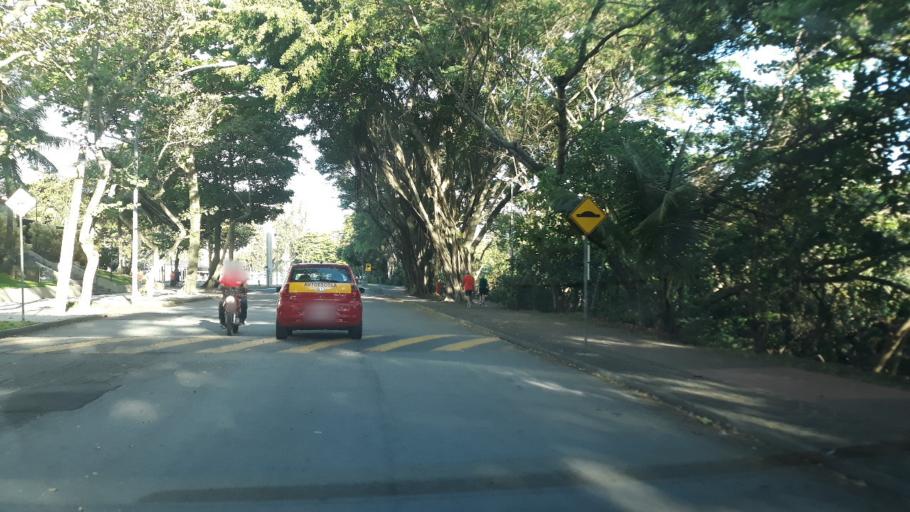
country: BR
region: Rio de Janeiro
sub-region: Rio De Janeiro
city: Rio de Janeiro
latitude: -23.0056
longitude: -43.3485
